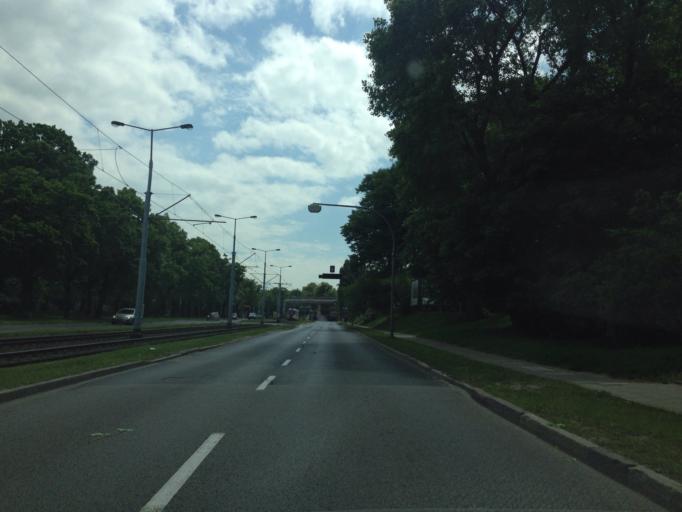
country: PL
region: Pomeranian Voivodeship
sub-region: Gdansk
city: Gdansk
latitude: 54.3783
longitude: 18.6226
